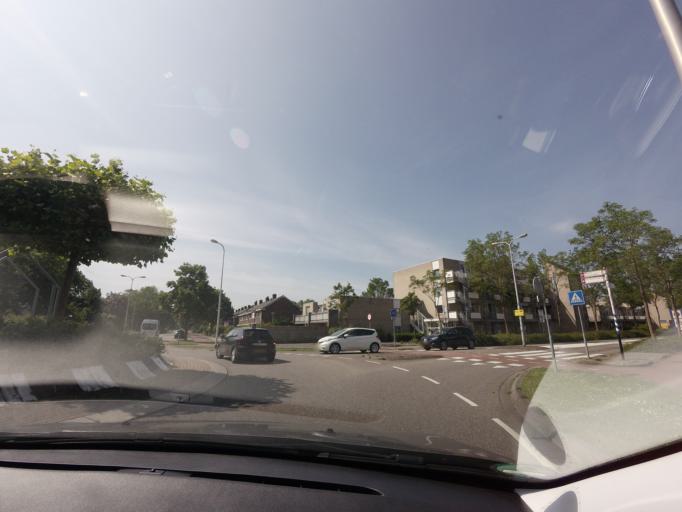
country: NL
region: South Holland
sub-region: Gemeente Barendrecht
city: Barendrecht
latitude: 51.8500
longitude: 4.5362
